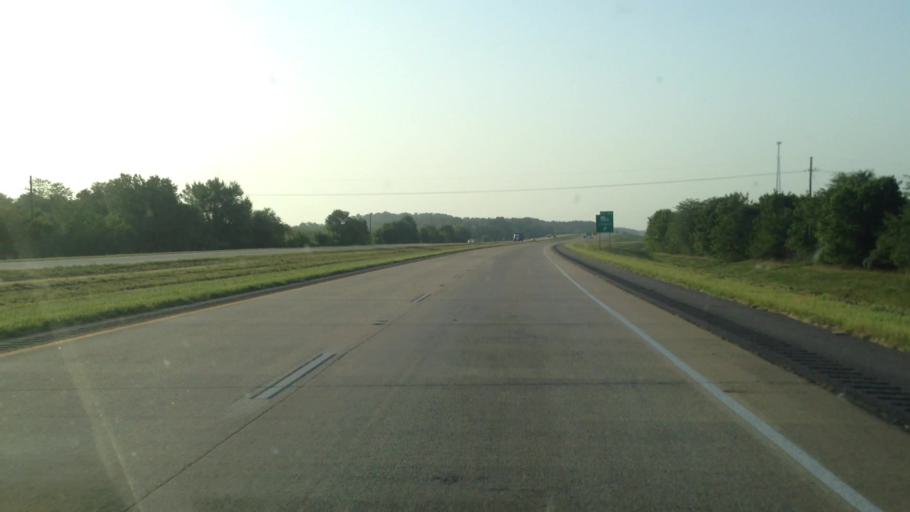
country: US
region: Louisiana
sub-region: Grant Parish
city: Colfax
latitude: 31.4998
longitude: -92.8694
